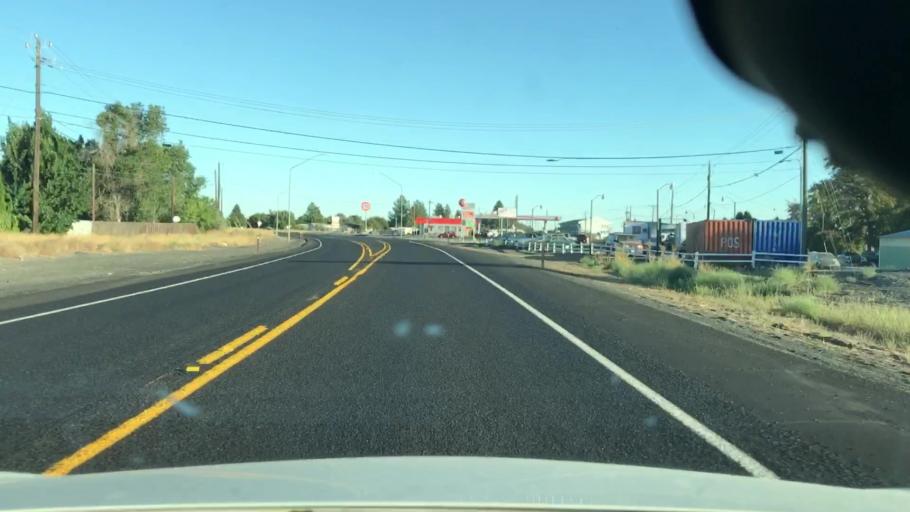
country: US
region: Washington
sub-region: Grant County
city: Cascade Valley
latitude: 47.1628
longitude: -119.3246
